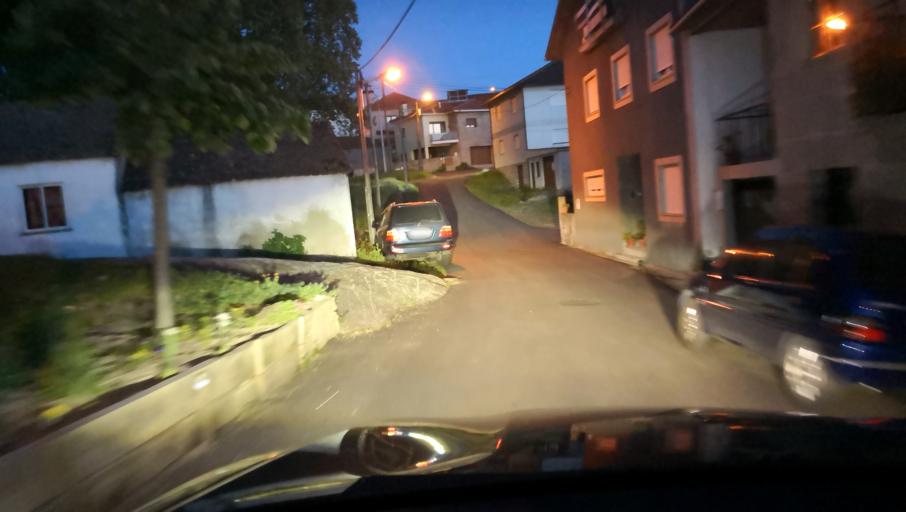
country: PT
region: Vila Real
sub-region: Vila Real
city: Vila Real
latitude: 41.3214
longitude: -7.6984
